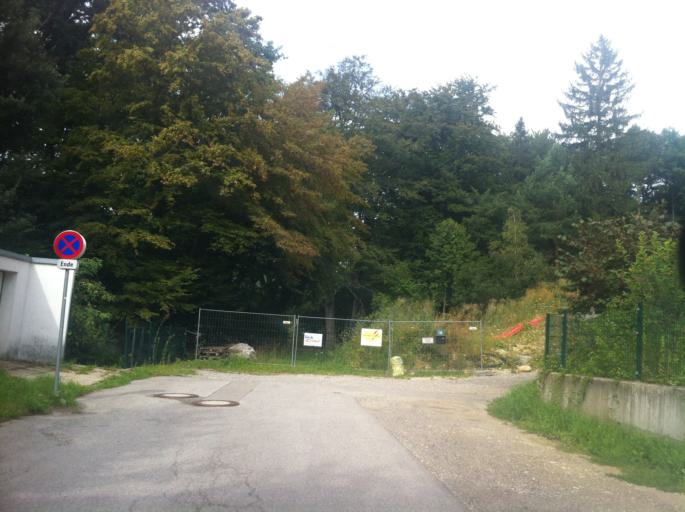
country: AT
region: Lower Austria
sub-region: Politischer Bezirk Wien-Umgebung
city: Purkersdorf
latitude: 48.2112
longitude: 16.1773
